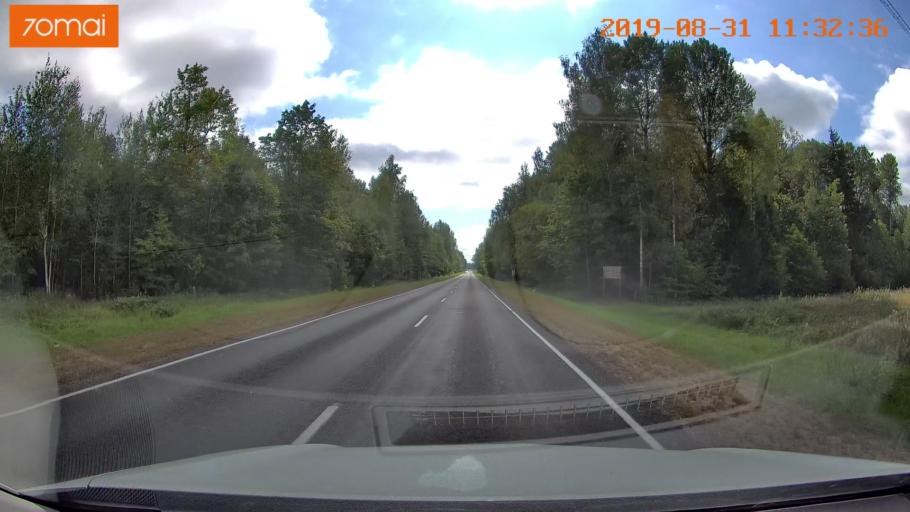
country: BY
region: Mogilev
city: Chavusy
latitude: 53.6913
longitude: 31.1633
